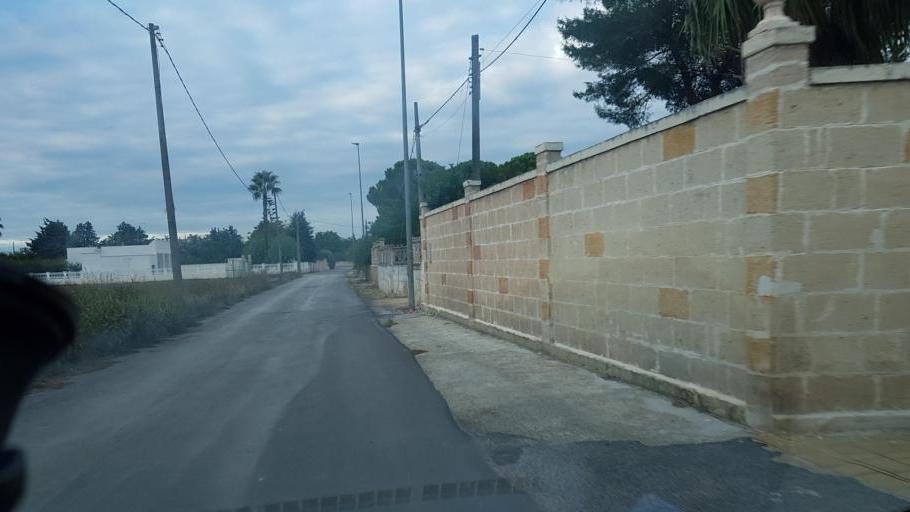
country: IT
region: Apulia
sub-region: Provincia di Brindisi
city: Oria
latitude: 40.5069
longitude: 17.6436
